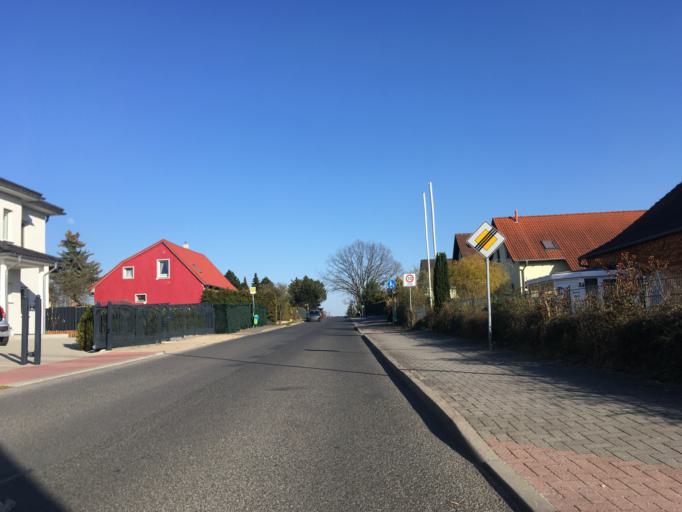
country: DE
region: Berlin
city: Falkenberg
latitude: 52.6011
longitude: 13.5534
